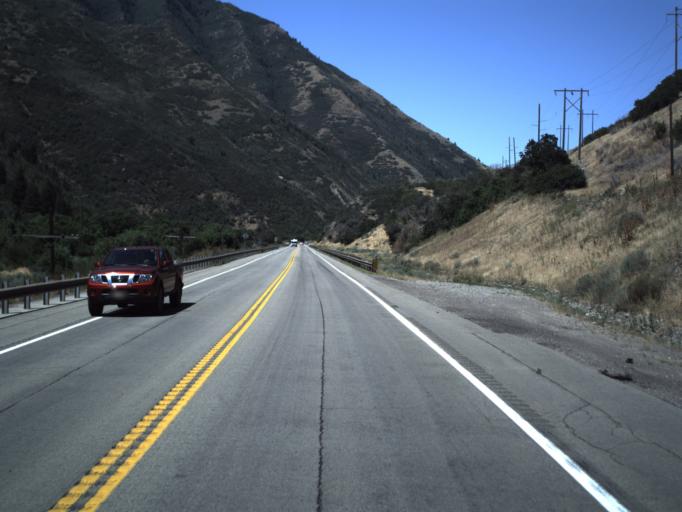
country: US
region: Utah
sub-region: Utah County
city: Mapleton
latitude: 40.0546
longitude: -111.5515
